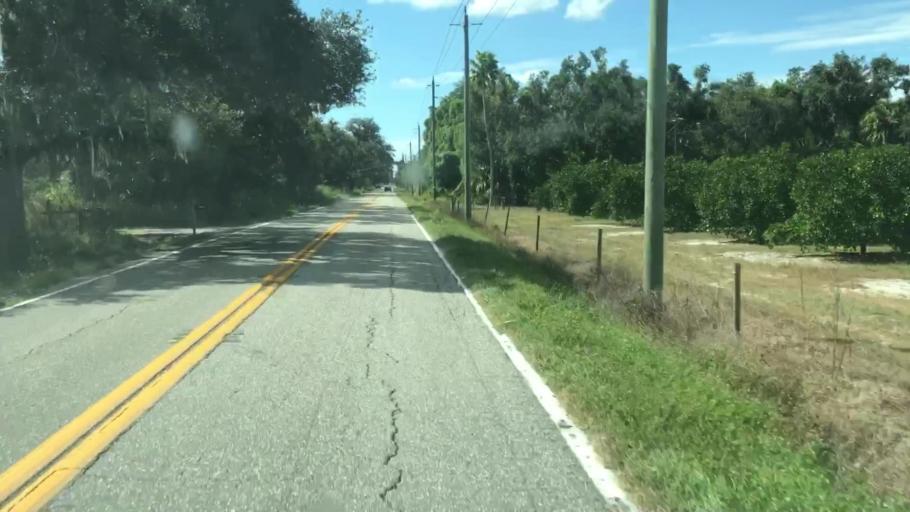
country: US
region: Florida
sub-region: Lee County
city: Alva
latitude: 26.7260
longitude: -81.6234
